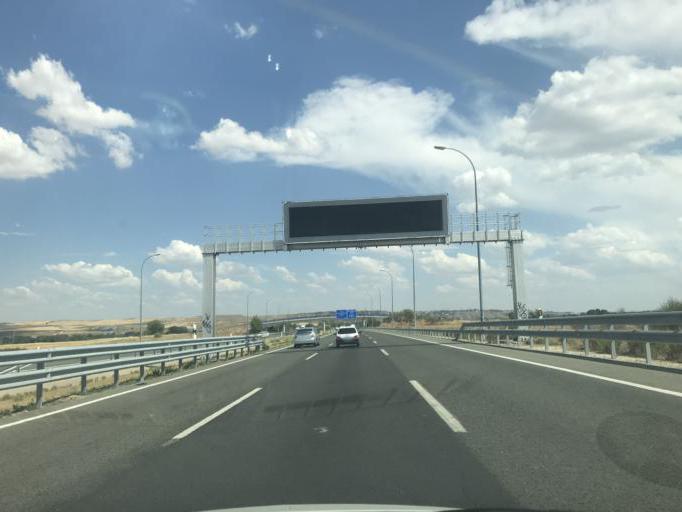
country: ES
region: Madrid
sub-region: Provincia de Madrid
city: San Sebastian de los Reyes
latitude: 40.5512
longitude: -3.5808
